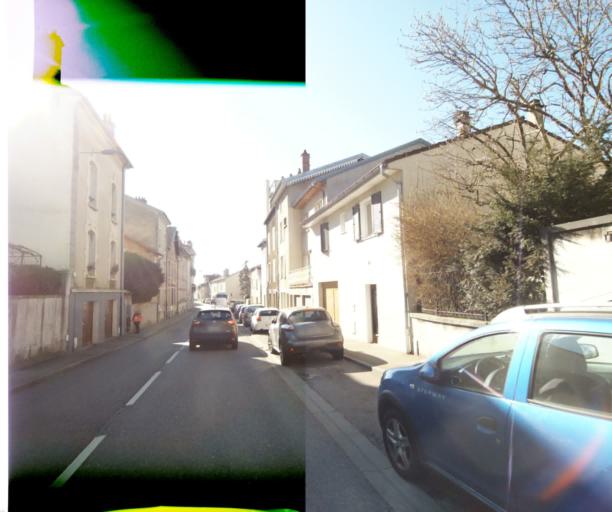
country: FR
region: Lorraine
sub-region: Departement de Meurthe-et-Moselle
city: Malzeville
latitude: 48.7124
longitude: 6.1844
